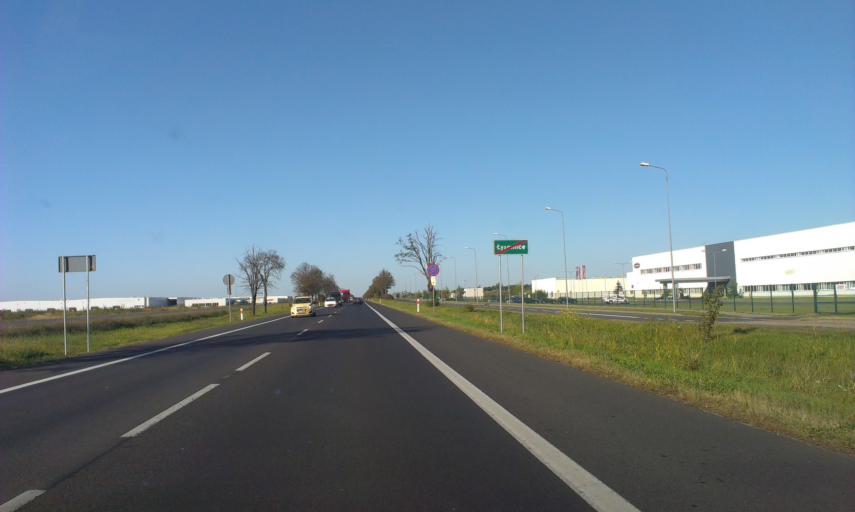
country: PL
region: Kujawsko-Pomorskie
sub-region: Powiat torunski
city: Lysomice
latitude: 53.0984
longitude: 18.6223
